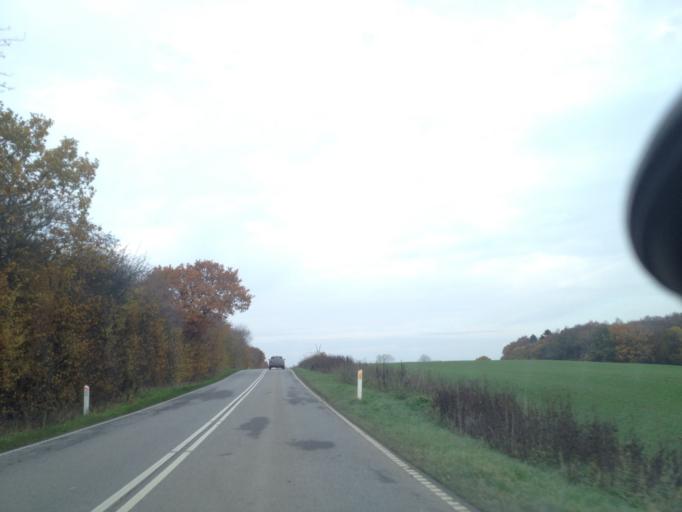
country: DK
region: South Denmark
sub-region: Assens Kommune
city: Vissenbjerg
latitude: 55.4507
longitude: 10.1224
